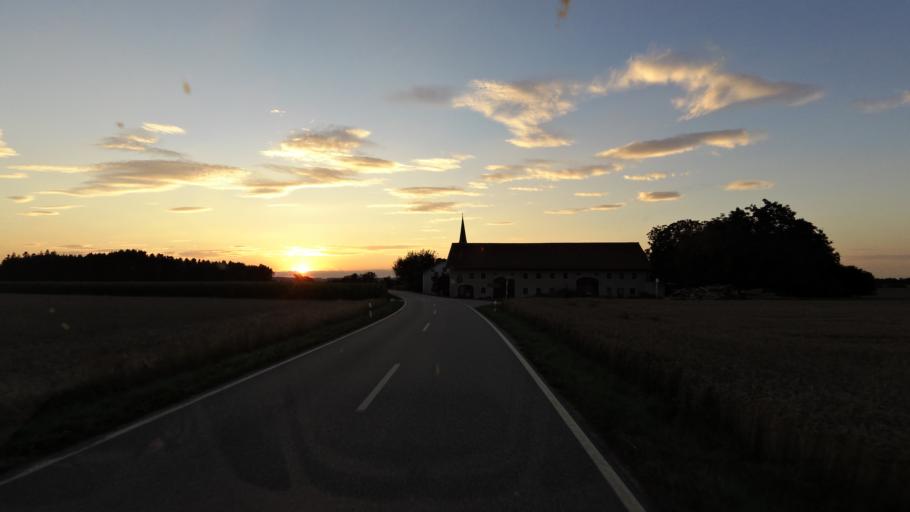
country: DE
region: Bavaria
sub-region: Upper Bavaria
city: Kraiburg am Inn
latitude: 48.1658
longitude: 12.4393
